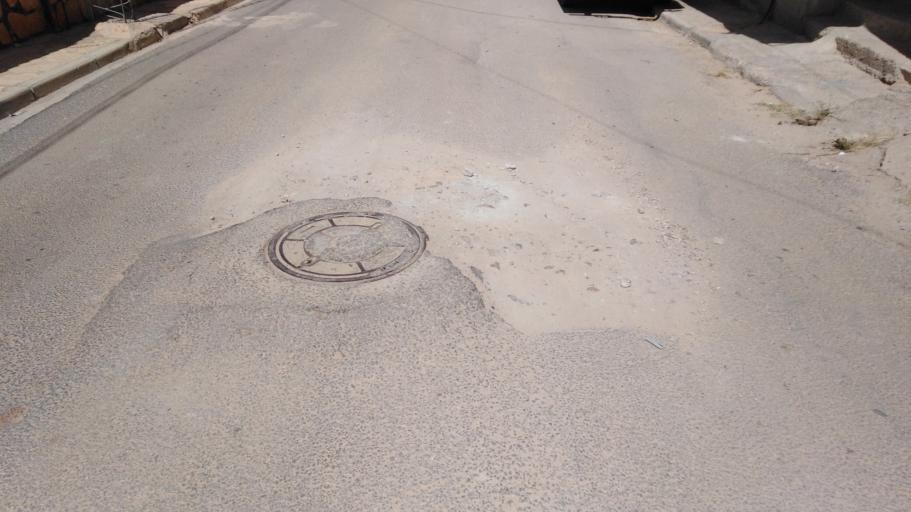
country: TN
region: Qabis
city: Gabes
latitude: 33.6207
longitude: 10.2808
